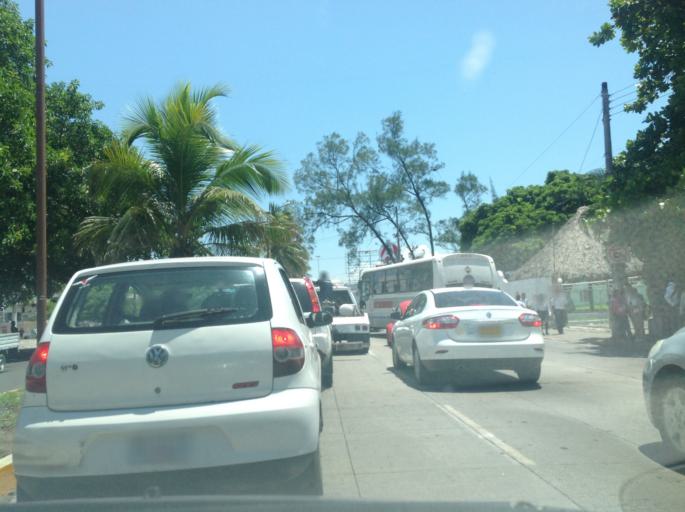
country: MX
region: Veracruz
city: Veracruz
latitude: 19.1508
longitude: -96.1298
